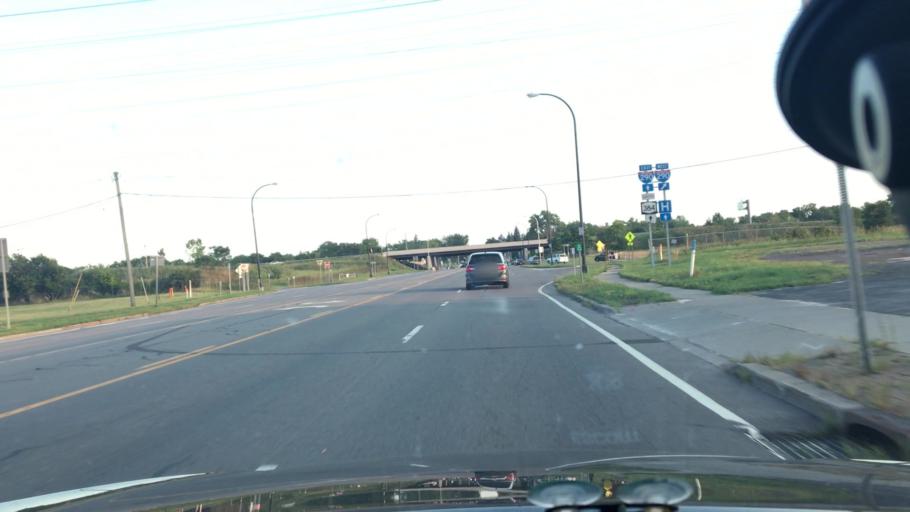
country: US
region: New York
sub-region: Erie County
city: Tonawanda
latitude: 42.9982
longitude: -78.8749
